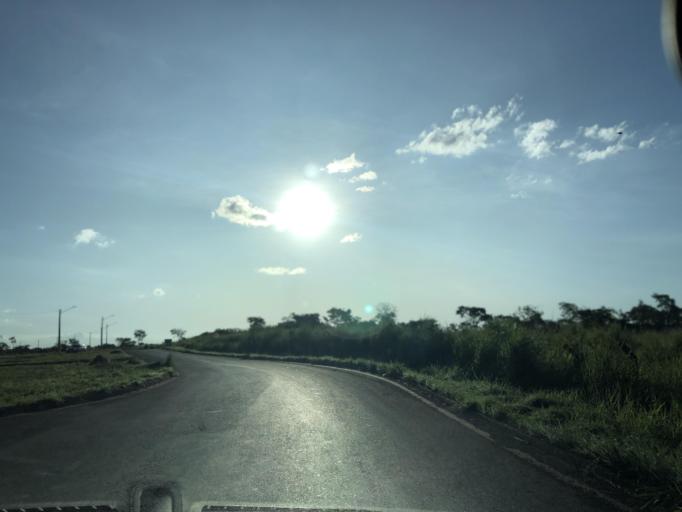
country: BR
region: Goias
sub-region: Luziania
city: Luziania
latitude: -16.2629
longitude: -47.9710
